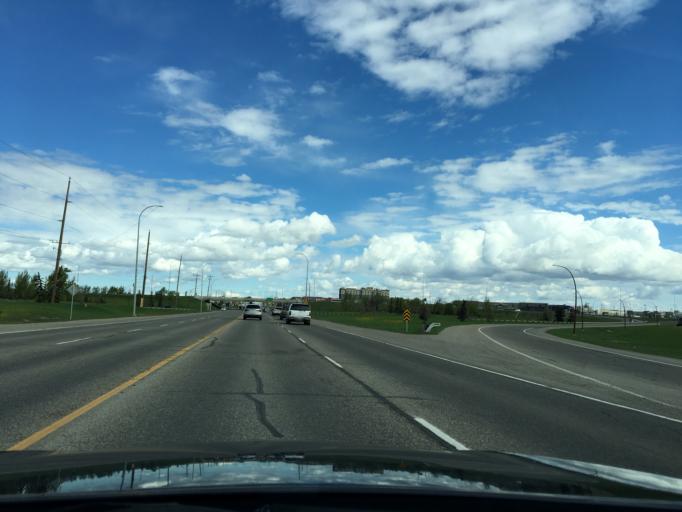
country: CA
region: Alberta
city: Calgary
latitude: 51.0636
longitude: -114.0017
